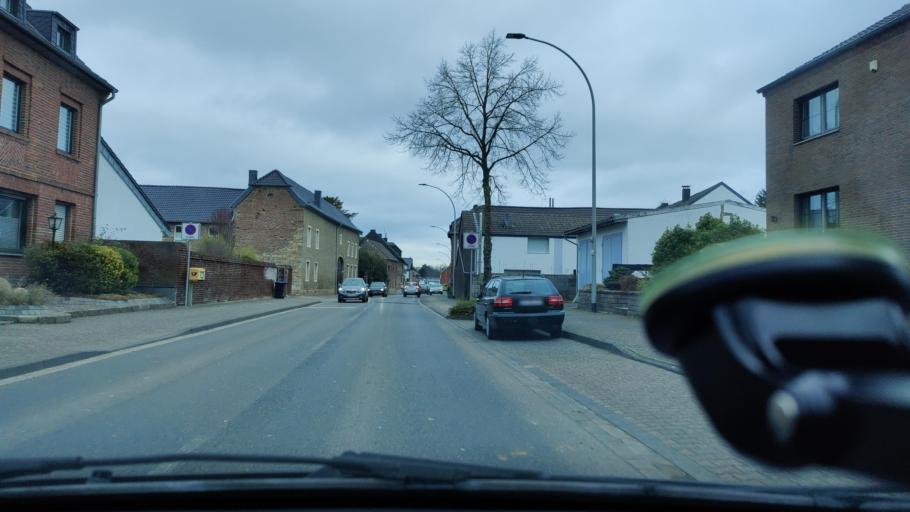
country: DE
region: North Rhine-Westphalia
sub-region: Regierungsbezirk Koln
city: Wurselen
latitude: 50.8337
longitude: 6.1723
